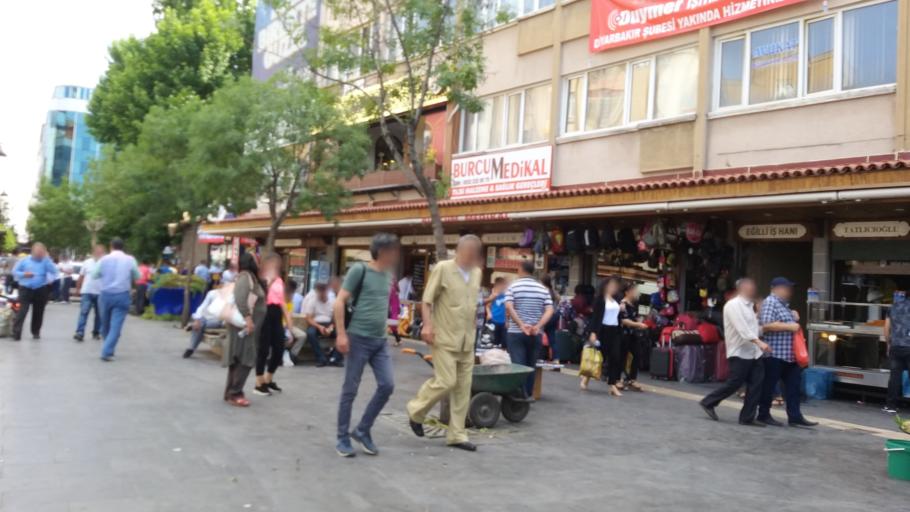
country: TR
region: Diyarbakir
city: Sur
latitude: 37.9157
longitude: 40.2367
